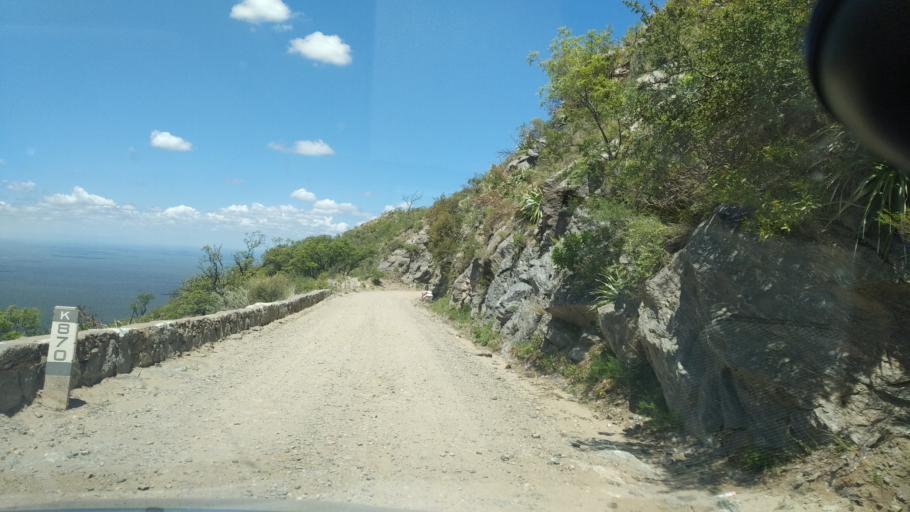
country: AR
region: Cordoba
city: Salsacate
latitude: -31.3790
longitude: -65.3990
